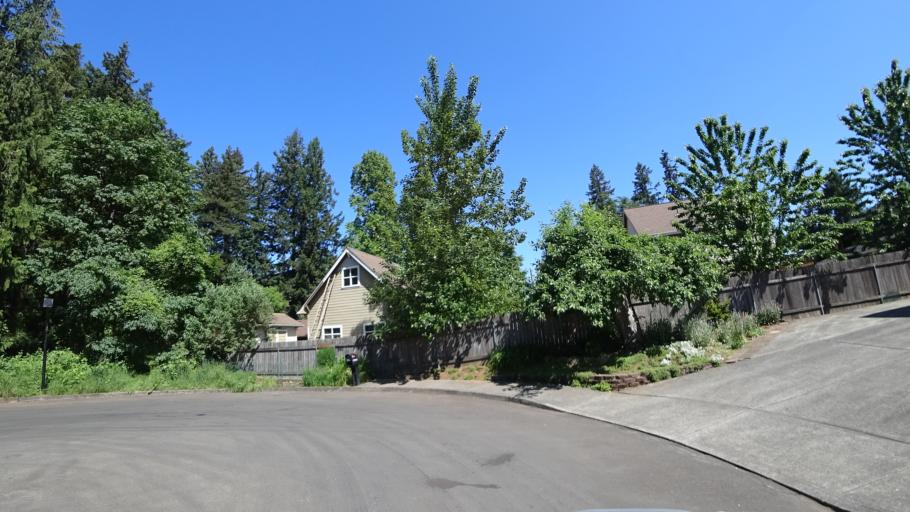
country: US
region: Oregon
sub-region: Clackamas County
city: Happy Valley
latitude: 45.4742
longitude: -122.5322
